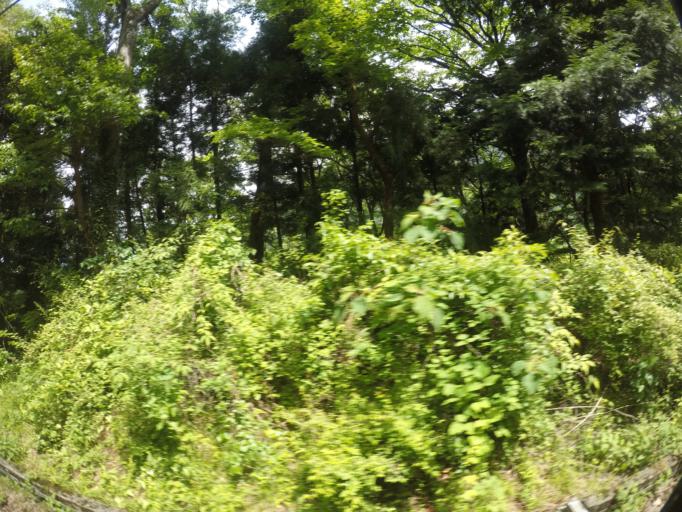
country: JP
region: Kanagawa
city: Hakone
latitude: 35.2430
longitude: 139.0608
